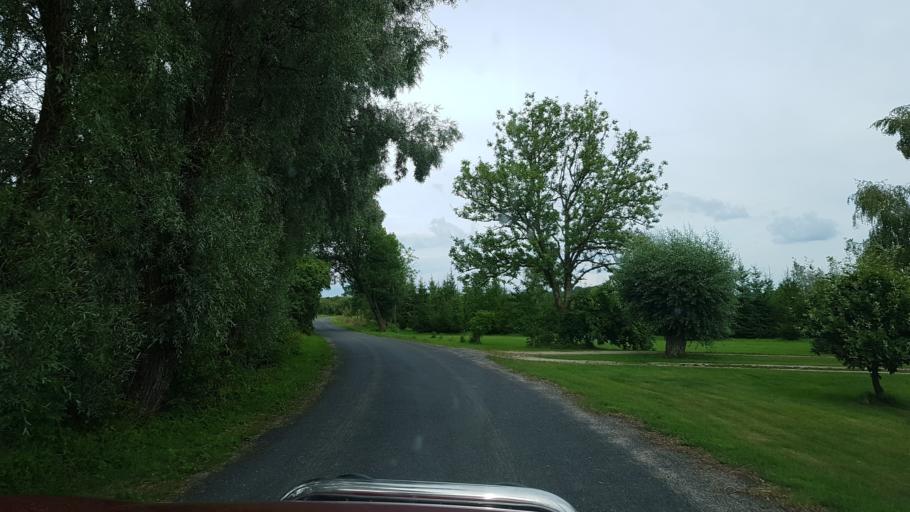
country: EE
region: Laeaene
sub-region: Ridala Parish
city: Uuemoisa
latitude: 58.9832
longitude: 23.8022
